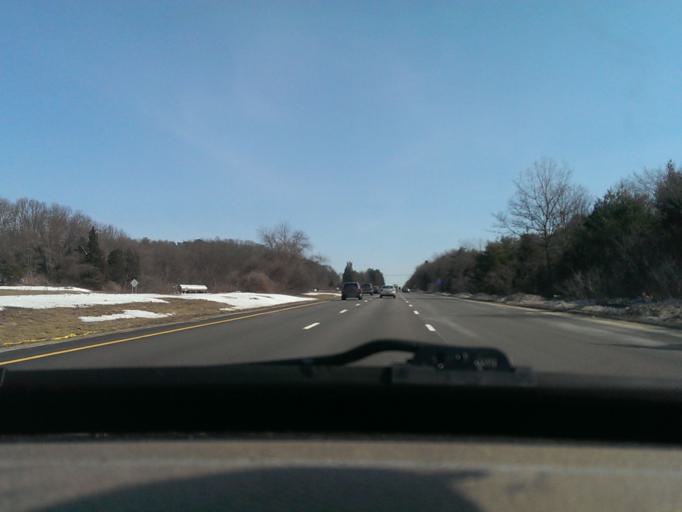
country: US
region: Massachusetts
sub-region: Bristol County
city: Seekonk
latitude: 41.8017
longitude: -71.3299
